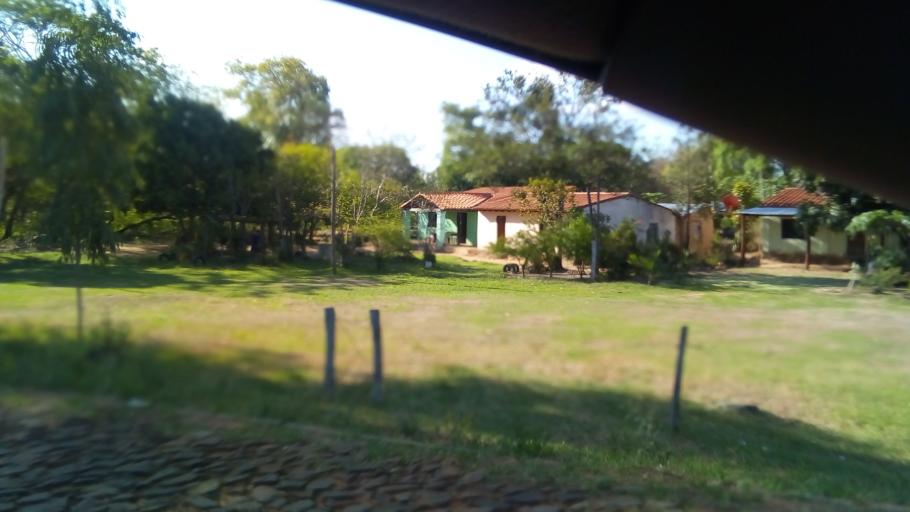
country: PY
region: Cordillera
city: Arroyos y Esteros
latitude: -24.9975
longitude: -57.1713
